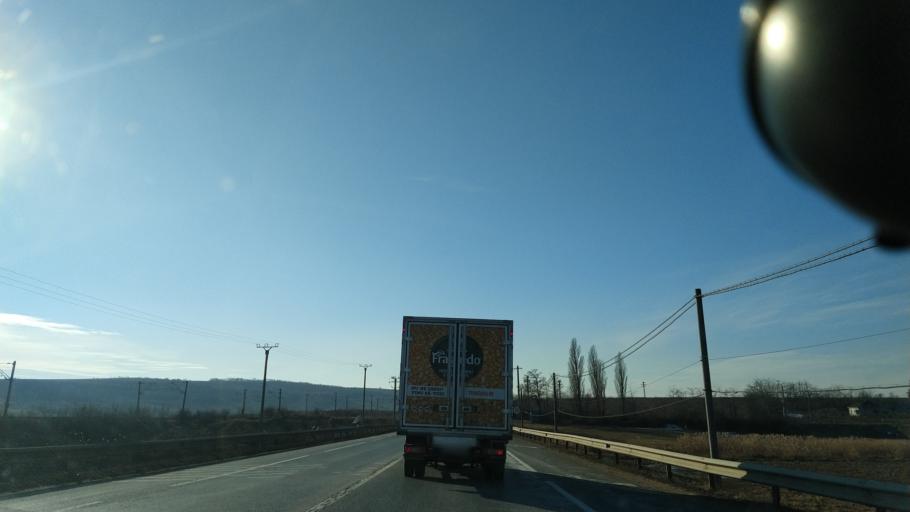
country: RO
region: Iasi
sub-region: Comuna Baltati
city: Baltati
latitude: 47.2243
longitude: 27.1794
